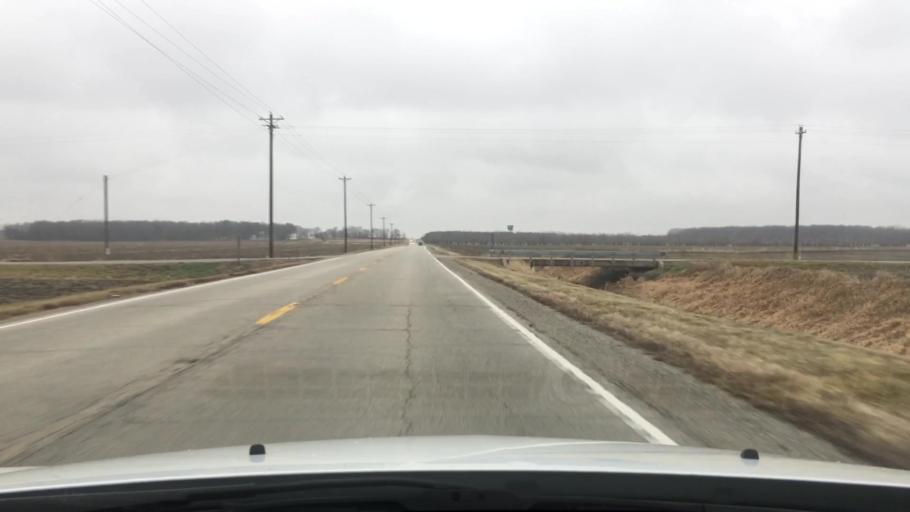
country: US
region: Illinois
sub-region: Iroquois County
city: Watseka
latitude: 40.8909
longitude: -87.6725
